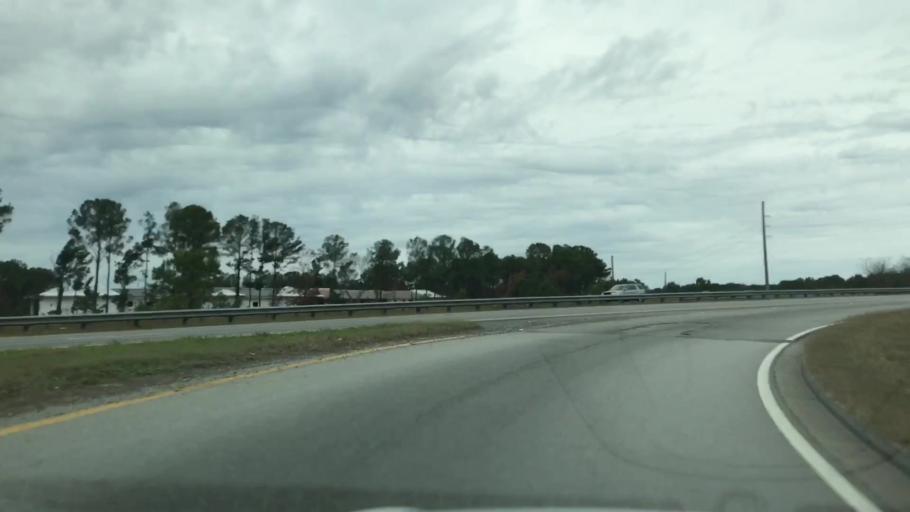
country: US
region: South Carolina
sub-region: Charleston County
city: Mount Pleasant
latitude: 32.8391
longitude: -79.8608
